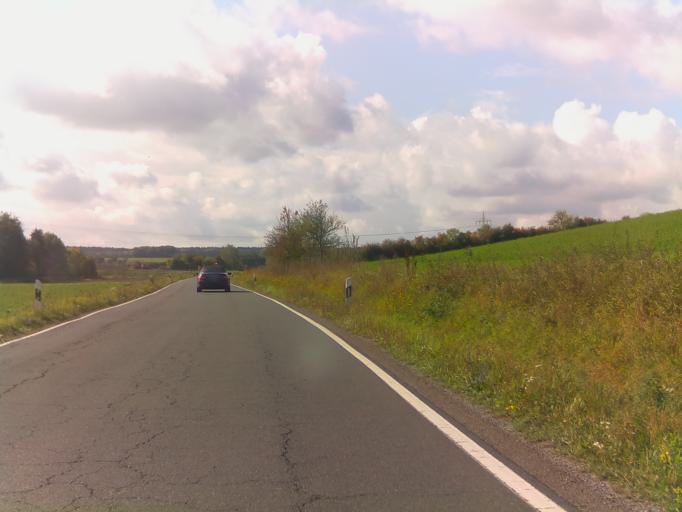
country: DE
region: Bavaria
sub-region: Regierungsbezirk Unterfranken
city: Biebelried
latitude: 49.7349
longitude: 10.1003
